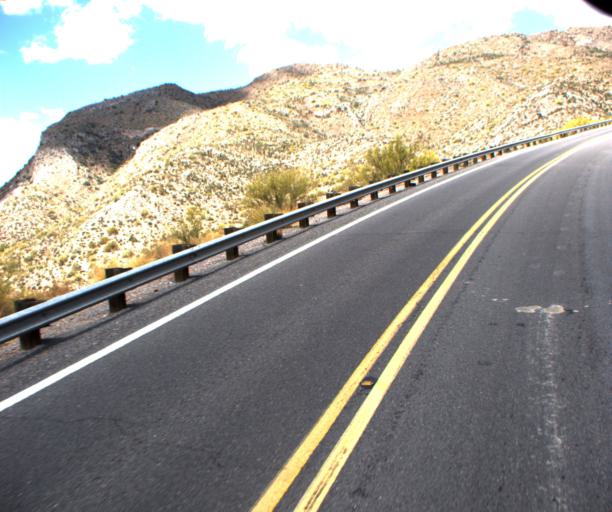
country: US
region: Arizona
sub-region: Pinal County
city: Superior
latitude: 33.1920
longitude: -111.0512
